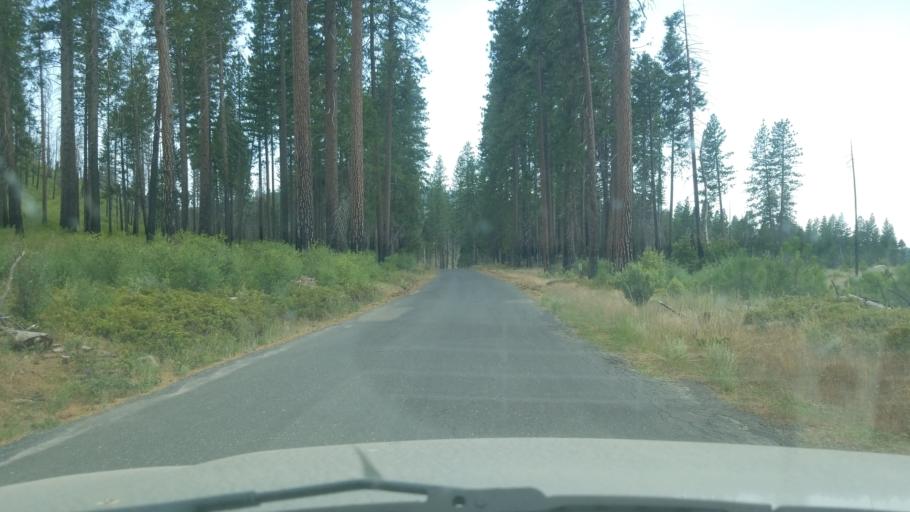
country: US
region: California
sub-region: Mariposa County
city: Yosemite Valley
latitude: 37.8714
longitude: -119.8641
